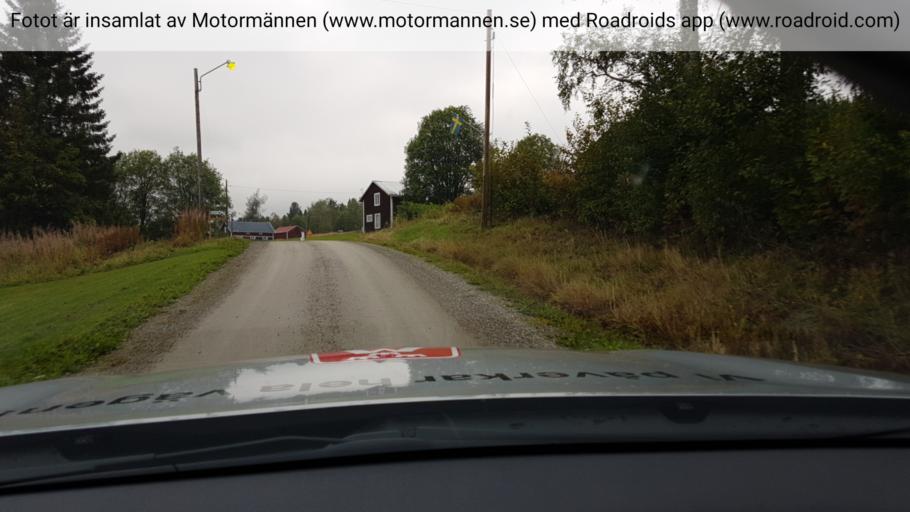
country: SE
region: Jaemtland
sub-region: Braecke Kommun
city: Braecke
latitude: 62.7639
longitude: 15.4986
